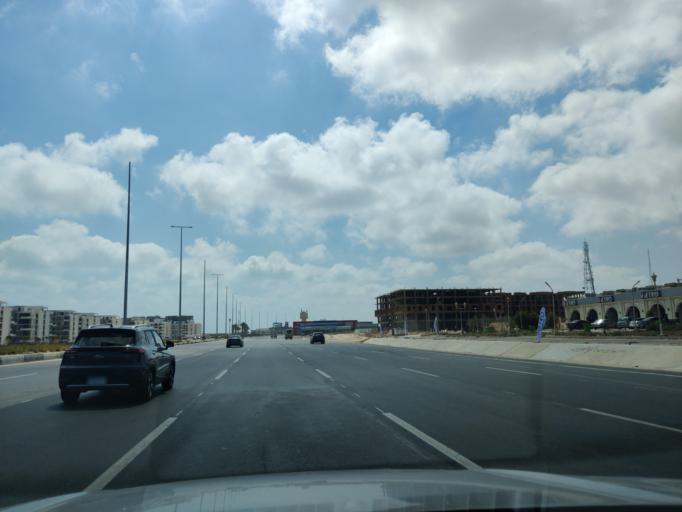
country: EG
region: Muhafazat Matruh
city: Al `Alamayn
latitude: 30.8455
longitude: 28.9367
